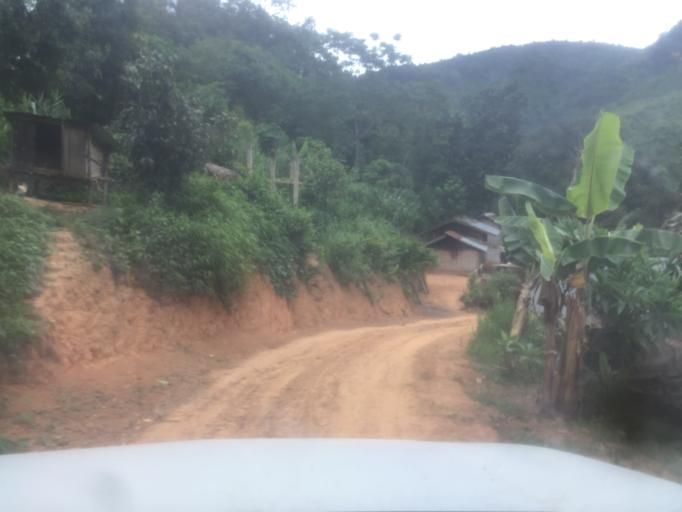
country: LA
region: Phongsali
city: Khoa
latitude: 20.9139
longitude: 102.5609
